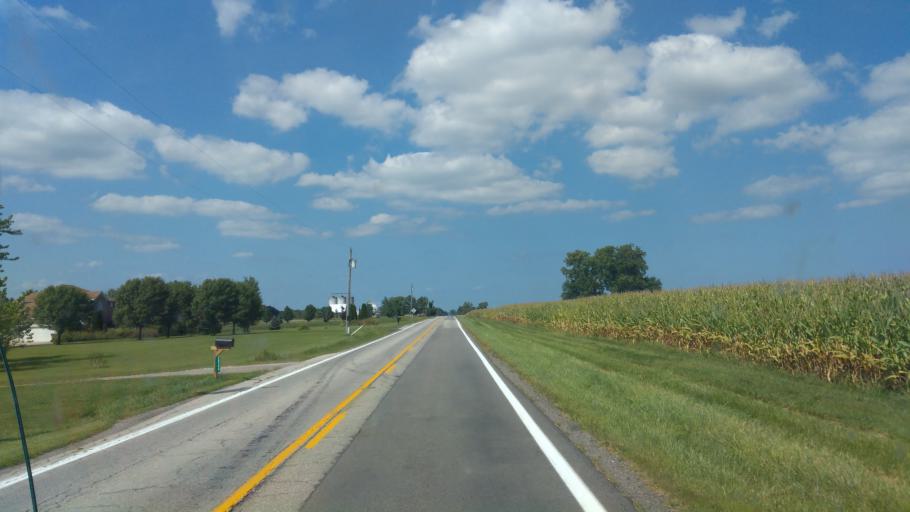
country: US
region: Ohio
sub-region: Union County
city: Marysville
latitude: 40.3552
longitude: -83.4549
